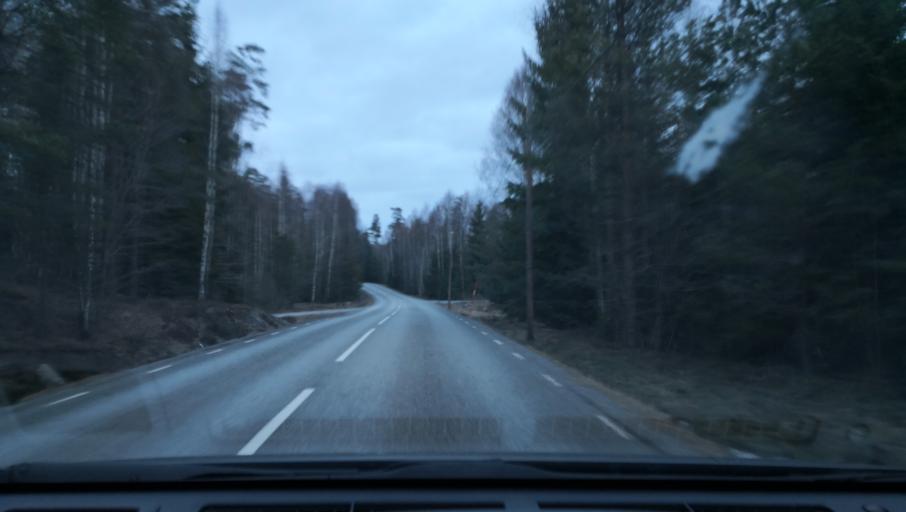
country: SE
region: Vaestmanland
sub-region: Kopings Kommun
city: Kolsva
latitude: 59.5776
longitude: 15.8018
